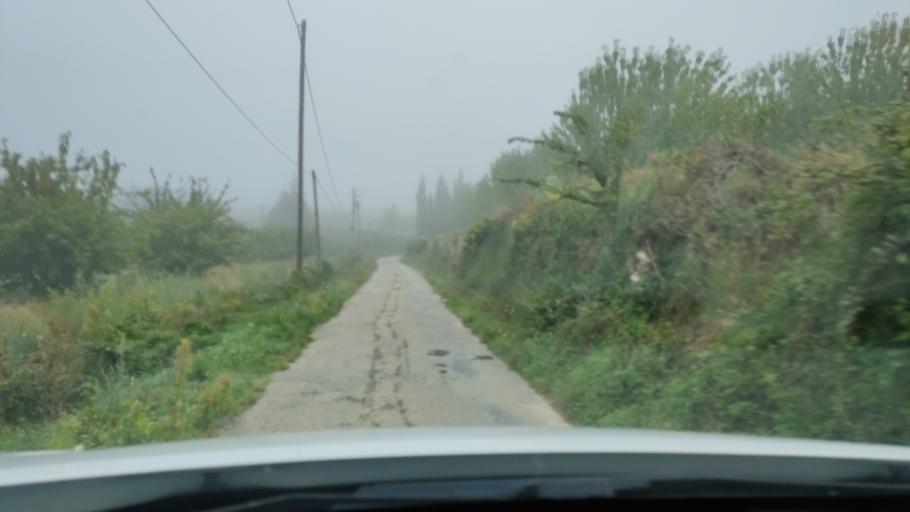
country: FR
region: Provence-Alpes-Cote d'Azur
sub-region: Departement du Vaucluse
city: Bonnieux
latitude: 43.8384
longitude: 5.3207
